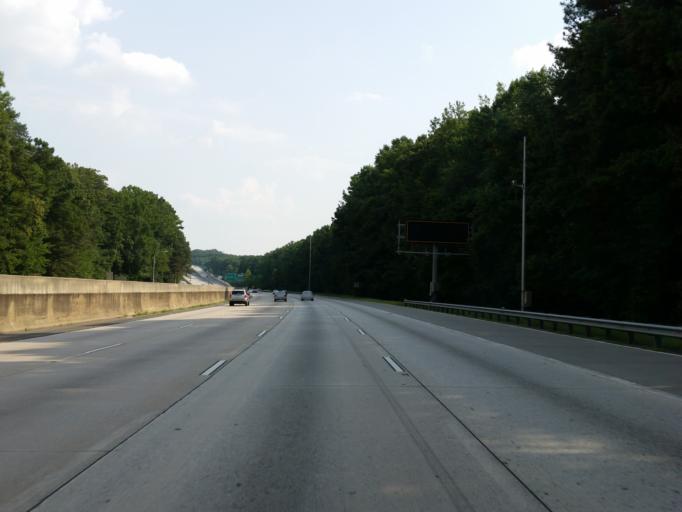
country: US
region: Georgia
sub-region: DeKalb County
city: Dunwoody
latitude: 33.9548
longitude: -84.3573
